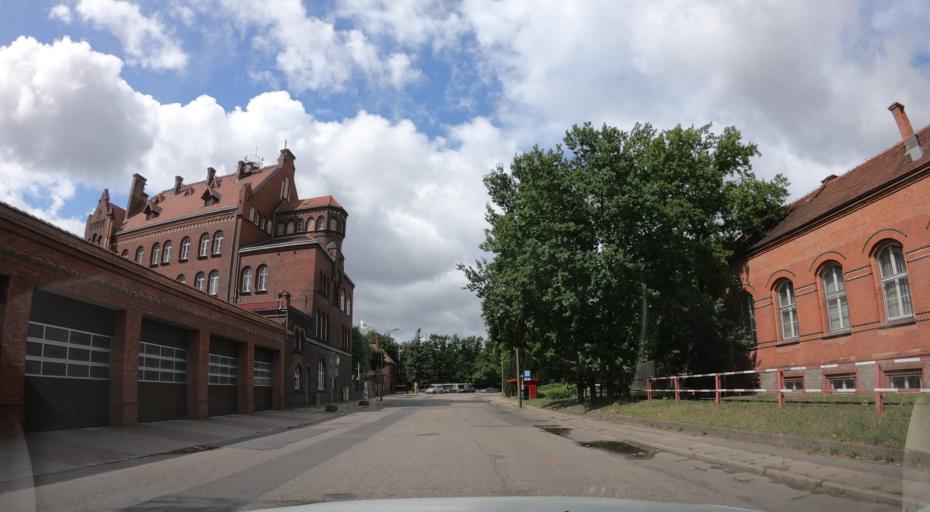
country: PL
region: West Pomeranian Voivodeship
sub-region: Szczecin
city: Szczecin
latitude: 53.4177
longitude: 14.5700
